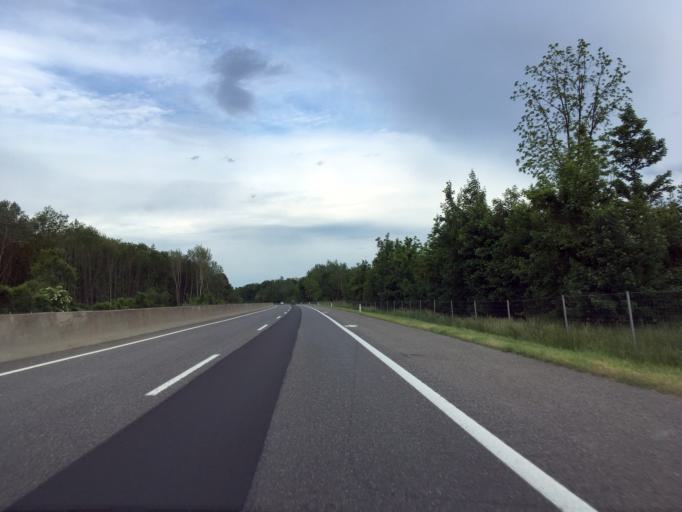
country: AT
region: Lower Austria
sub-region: Politischer Bezirk Tulln
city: Michelhausen
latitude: 48.3704
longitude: 15.9392
